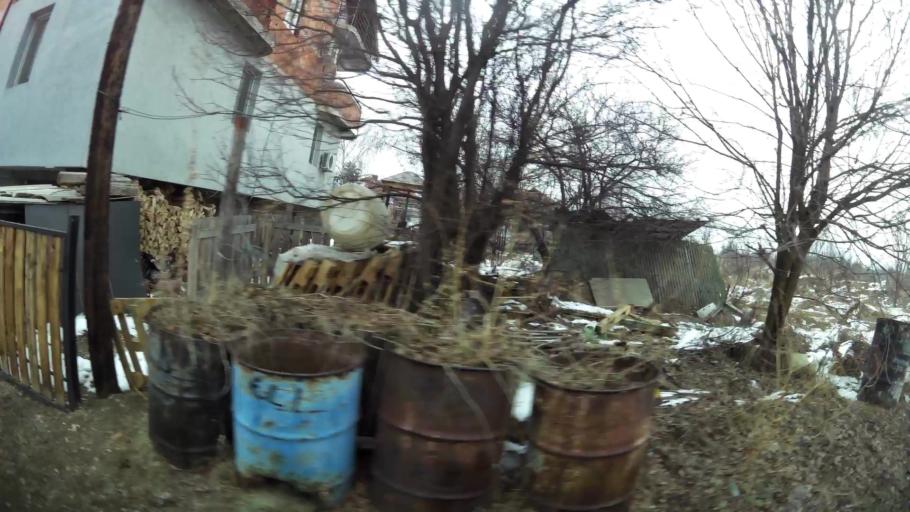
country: MK
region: Butel
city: Butel
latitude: 42.0353
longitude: 21.4509
